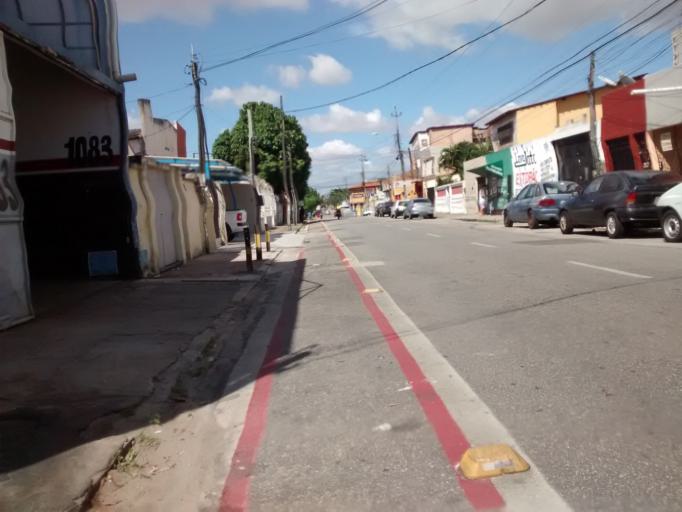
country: BR
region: Ceara
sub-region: Fortaleza
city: Fortaleza
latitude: -3.7295
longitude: -38.5518
